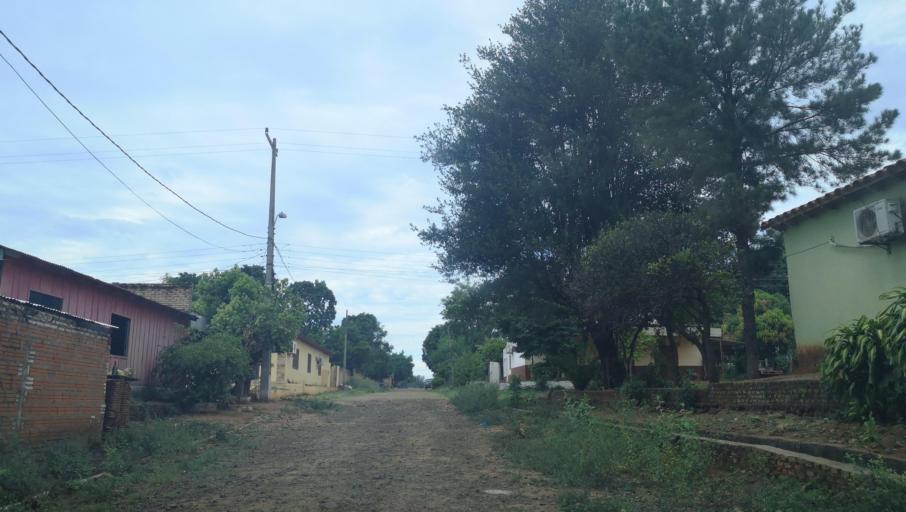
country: PY
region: San Pedro
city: Capiibary
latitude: -24.7321
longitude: -56.0220
